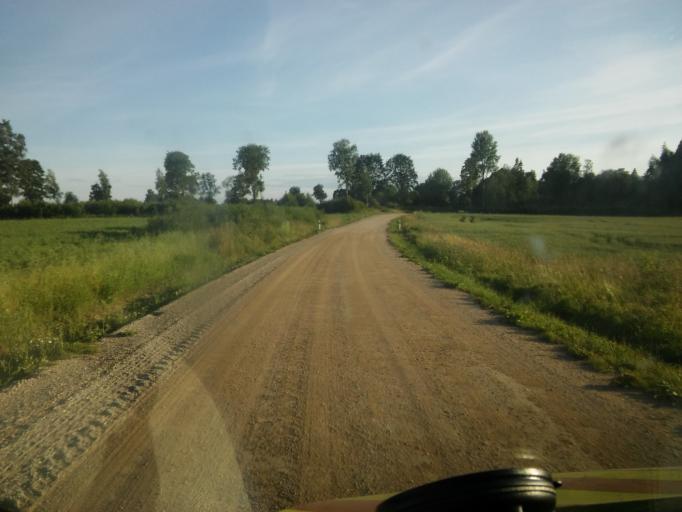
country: EE
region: Valgamaa
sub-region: Torva linn
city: Torva
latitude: 58.0380
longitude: 25.8992
